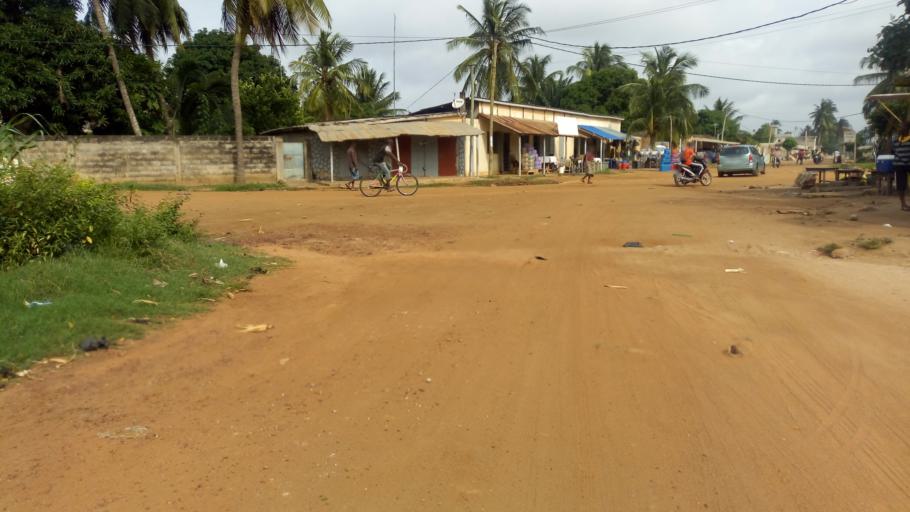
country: TG
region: Maritime
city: Lome
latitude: 6.1761
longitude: 1.1692
